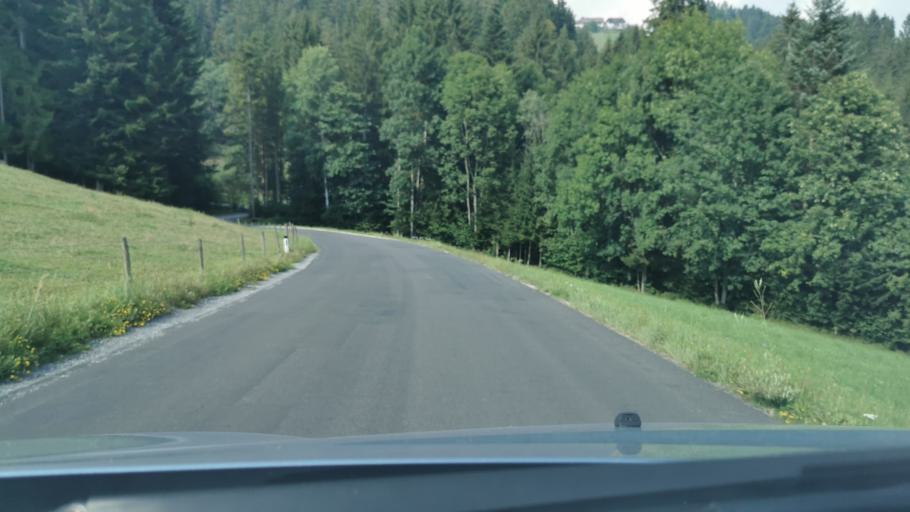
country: AT
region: Styria
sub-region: Politischer Bezirk Weiz
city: Strallegg
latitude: 47.3989
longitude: 15.6861
